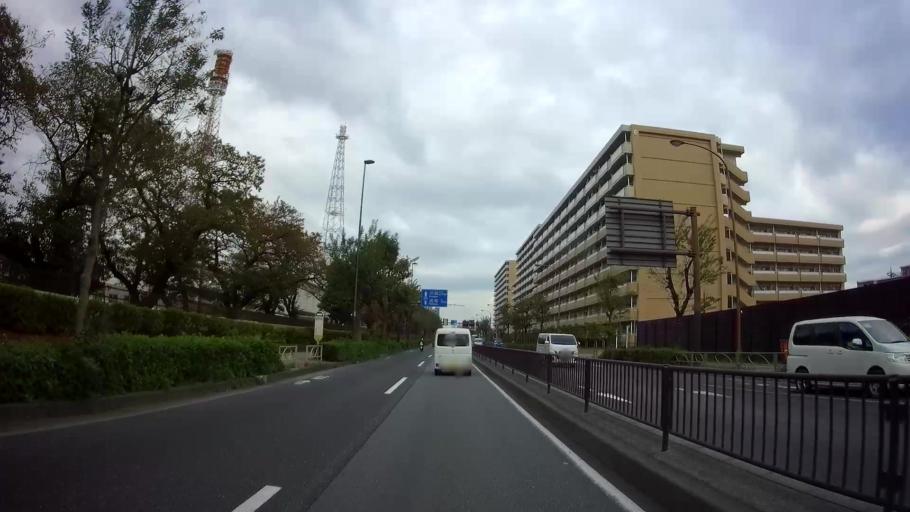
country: JP
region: Saitama
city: Wako
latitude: 35.7643
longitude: 139.6633
